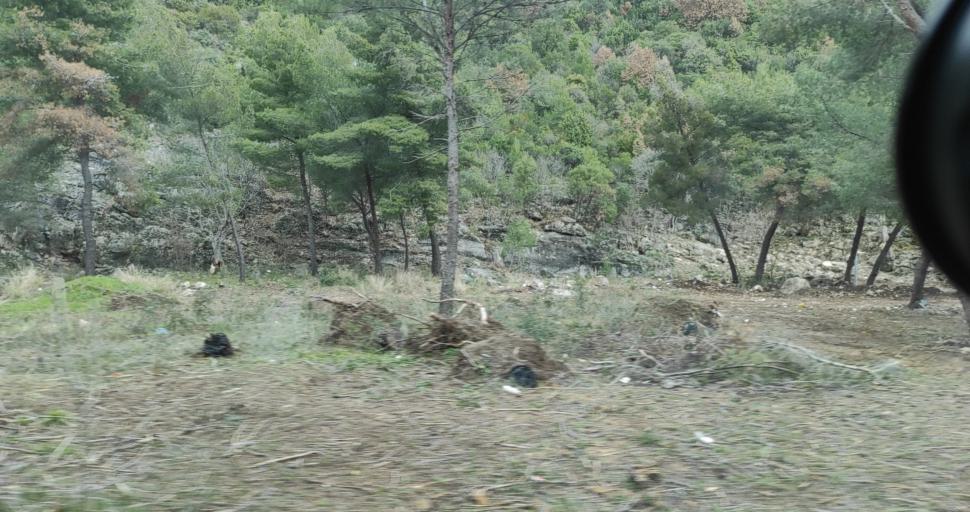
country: AL
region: Lezhe
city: Shengjin
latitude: 41.8233
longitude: 19.5608
